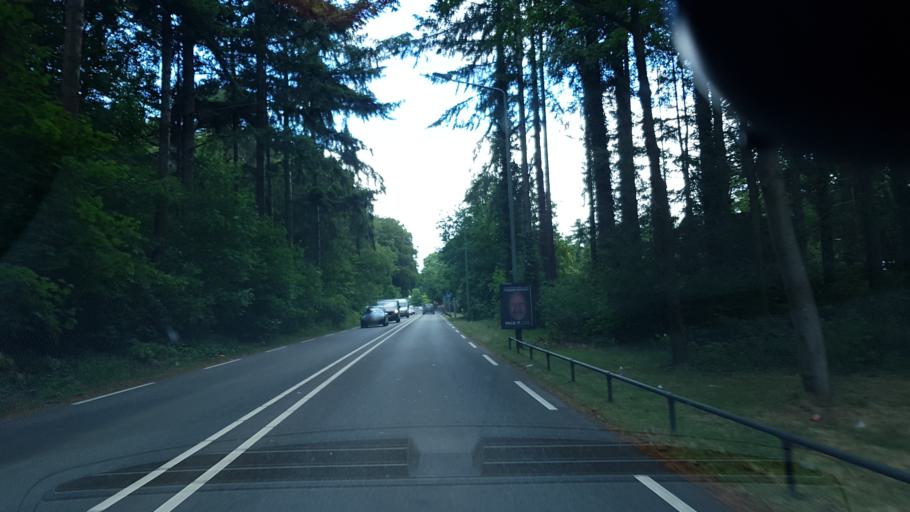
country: NL
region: North Holland
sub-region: Gemeente Hilversum
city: Hilversum
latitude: 52.2296
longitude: 5.1561
